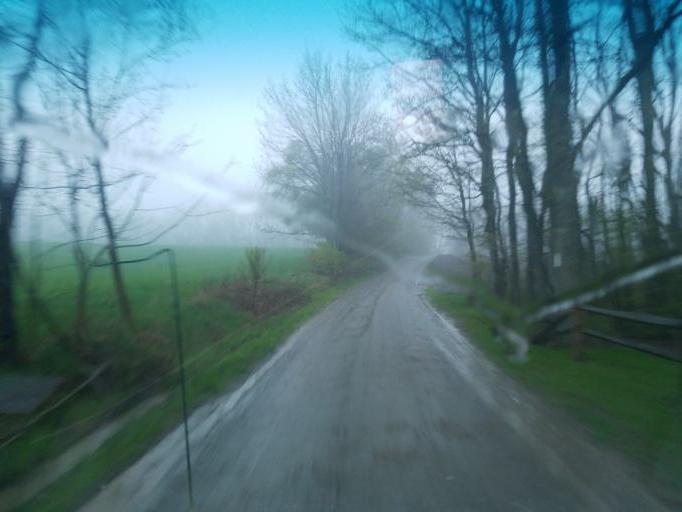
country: US
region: Pennsylvania
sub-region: Tioga County
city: Westfield
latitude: 41.9329
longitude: -77.7173
